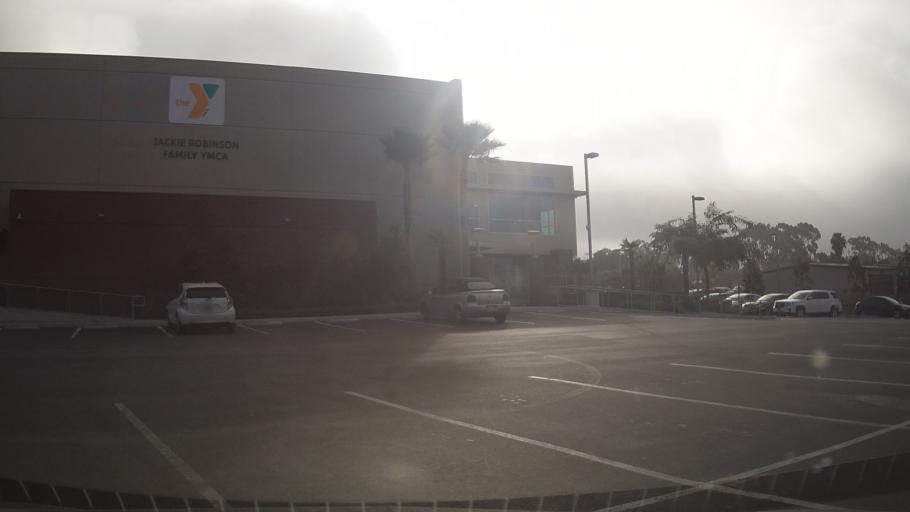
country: US
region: California
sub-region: San Diego County
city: National City
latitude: 32.7053
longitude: -117.0983
